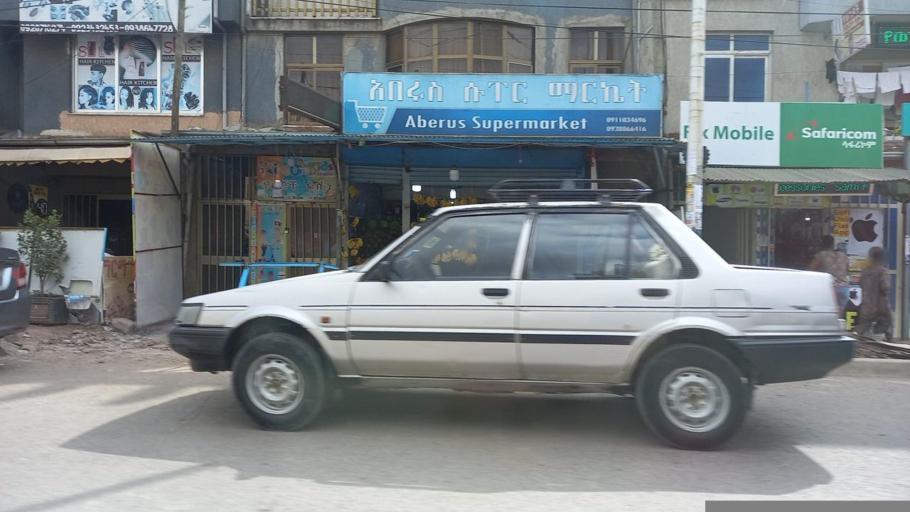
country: ET
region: Adis Abeba
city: Addis Ababa
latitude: 9.0098
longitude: 38.8551
